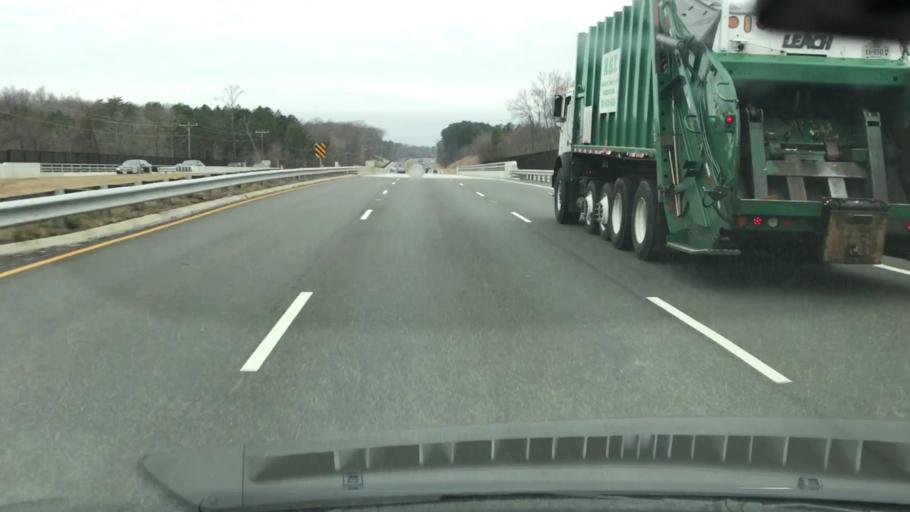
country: US
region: Virginia
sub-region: Fairfax County
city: Fort Belvoir
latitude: 38.7081
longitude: -77.1674
